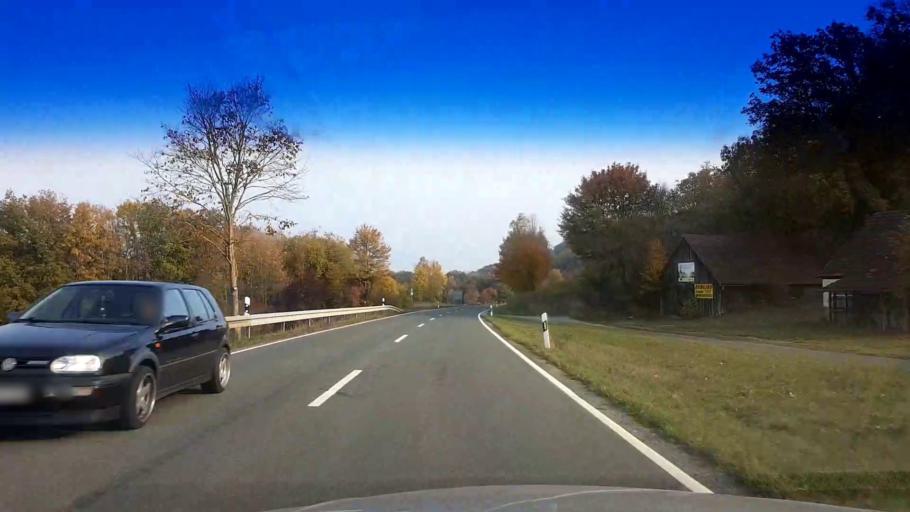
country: DE
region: Bavaria
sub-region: Upper Franconia
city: Weismain
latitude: 50.0659
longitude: 11.2215
